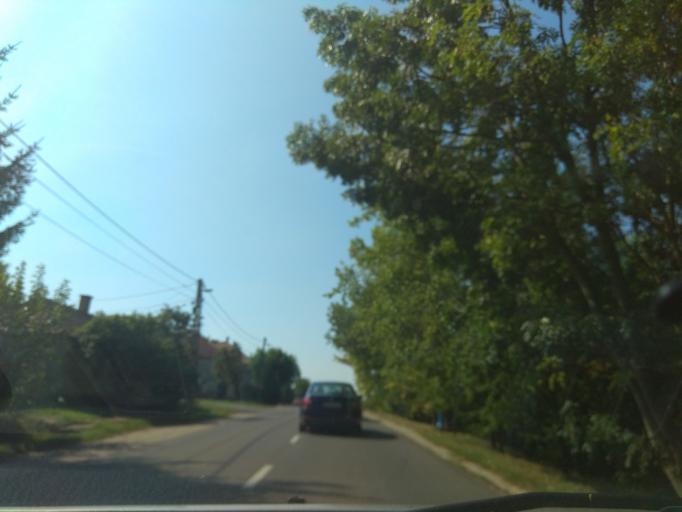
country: HU
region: Borsod-Abauj-Zemplen
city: Harsany
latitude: 47.9588
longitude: 20.7437
